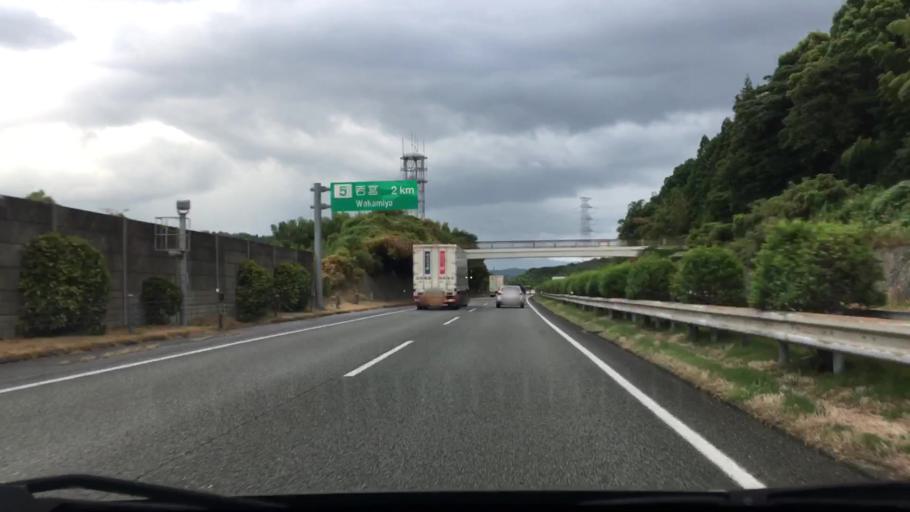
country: JP
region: Fukuoka
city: Miyata
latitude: 33.7502
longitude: 130.5852
